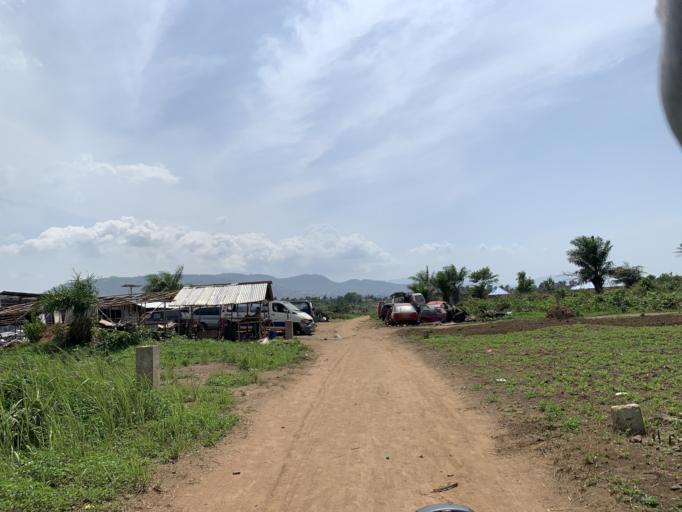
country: SL
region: Western Area
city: Waterloo
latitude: 8.3561
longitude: -13.0460
